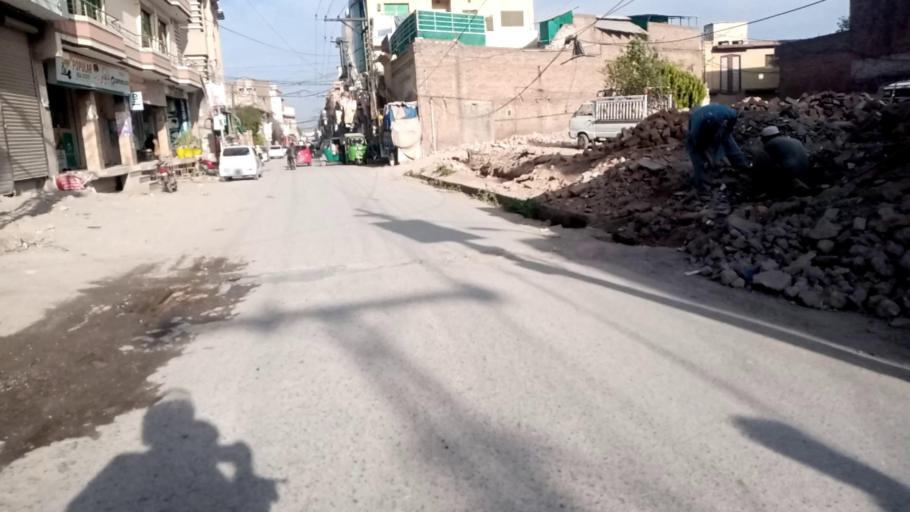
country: PK
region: Khyber Pakhtunkhwa
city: Peshawar
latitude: 34.0106
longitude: 71.6009
